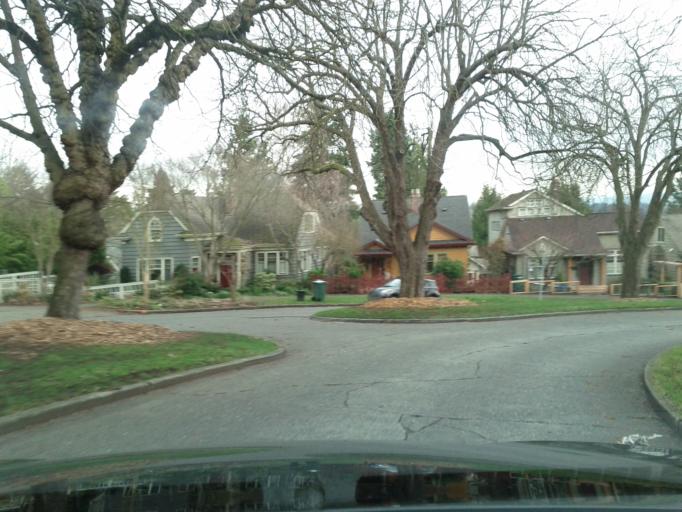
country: US
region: Washington
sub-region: King County
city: Seattle
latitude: 47.6704
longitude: -122.3083
